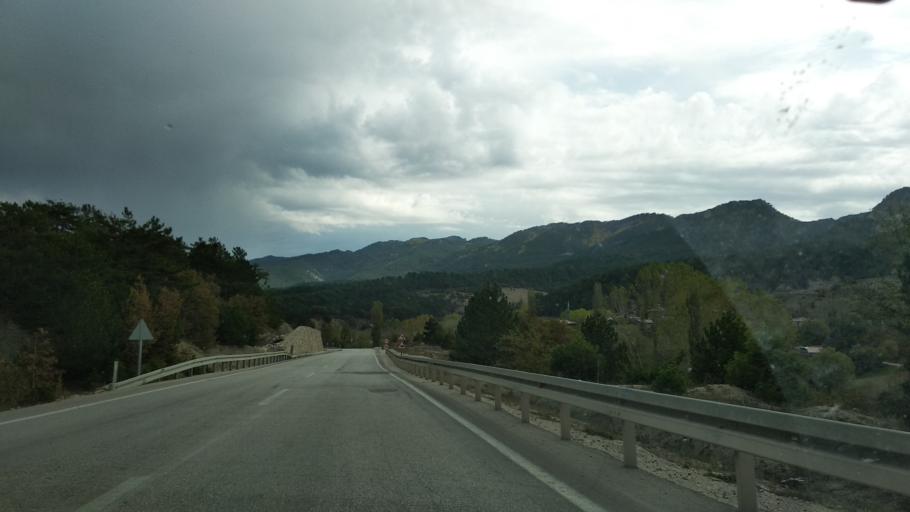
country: TR
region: Bolu
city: Mudurnu
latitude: 40.4372
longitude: 31.1536
